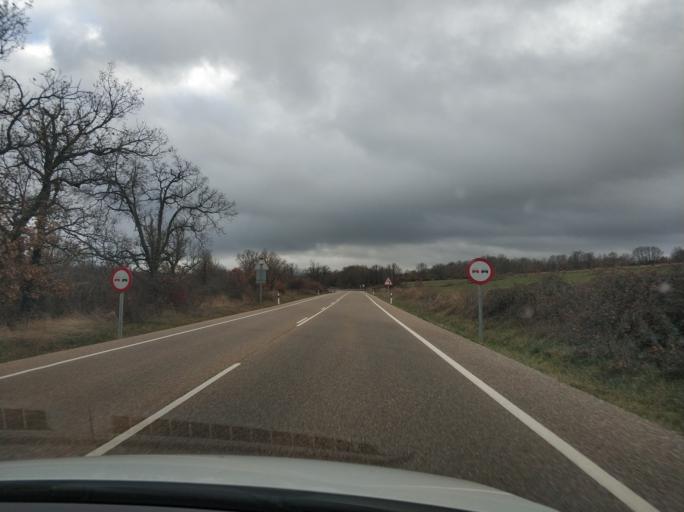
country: ES
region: Castille and Leon
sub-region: Provincia de Segovia
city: Riaza
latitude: 41.3030
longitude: -3.4778
